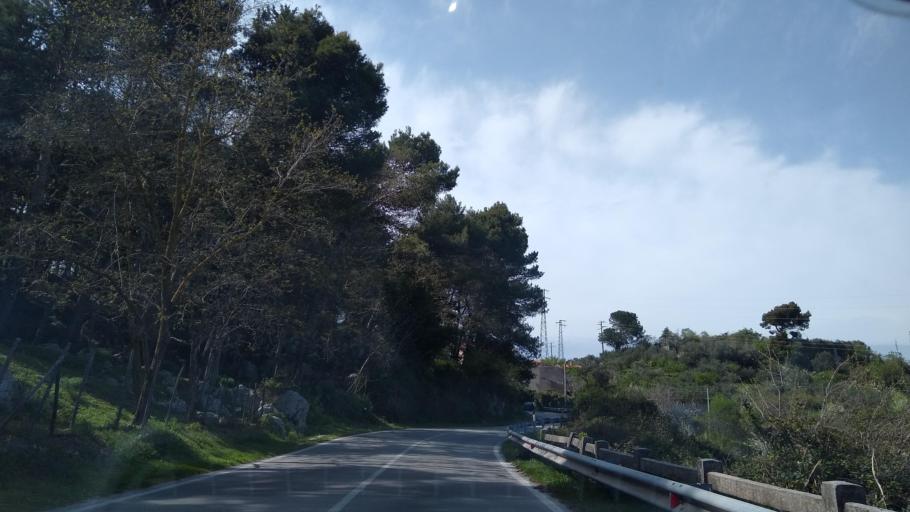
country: IT
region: Sicily
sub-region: Palermo
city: Pioppo
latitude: 38.0406
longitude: 13.2027
